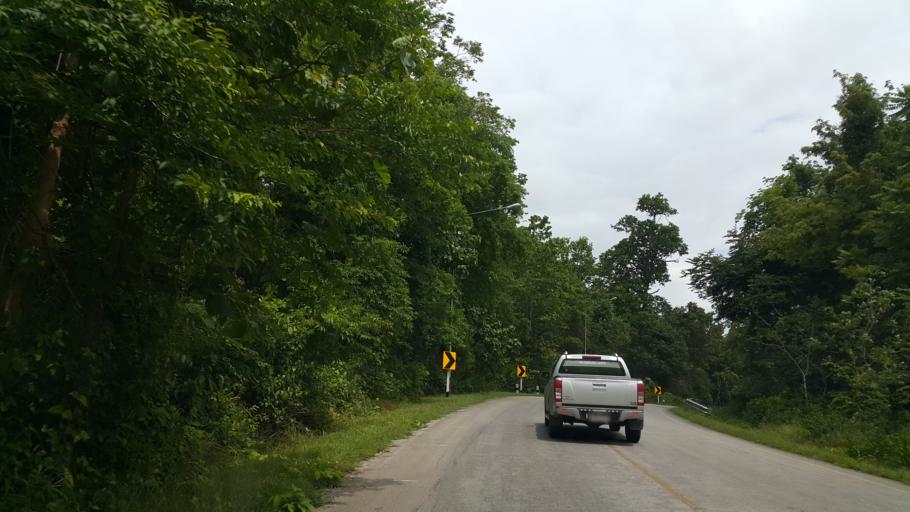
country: TH
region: Lampang
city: Mueang Pan
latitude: 18.7780
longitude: 99.5395
